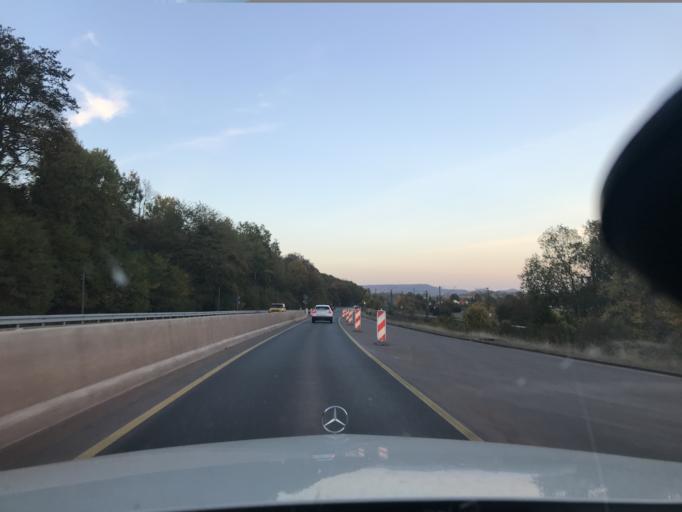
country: DE
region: Hesse
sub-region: Regierungsbezirk Kassel
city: Eschwege
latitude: 51.1480
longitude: 9.9795
